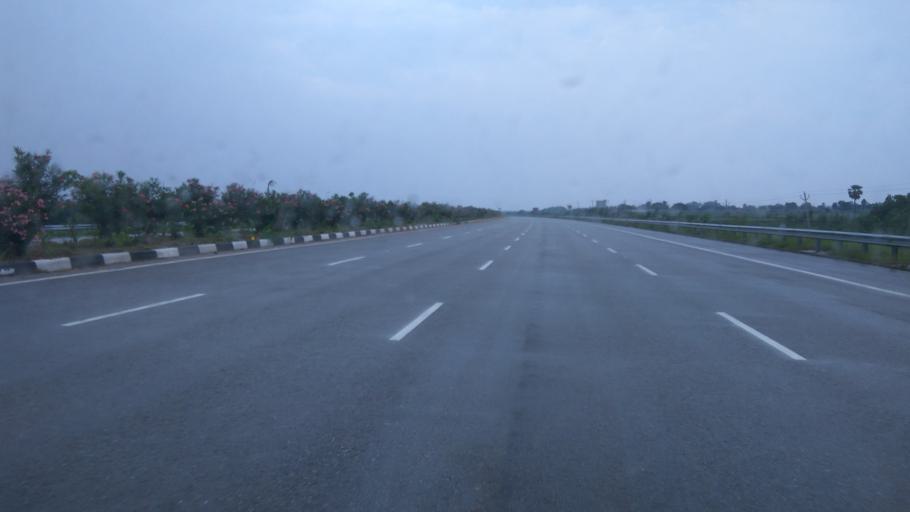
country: IN
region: Telangana
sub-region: Rangareddi
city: Ghatkesar
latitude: 17.4748
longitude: 78.6697
